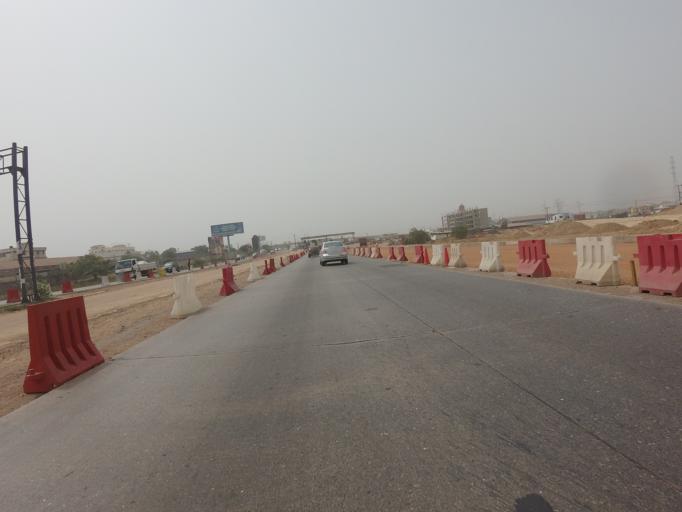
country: GH
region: Greater Accra
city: Tema
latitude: 5.6844
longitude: -0.0207
